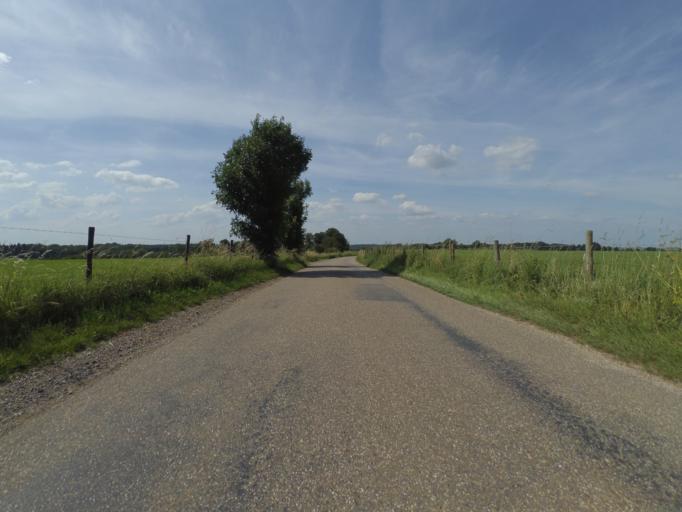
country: NL
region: Limburg
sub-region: Valkenburg aan de Geul
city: Schin op Geul
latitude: 50.7870
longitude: 5.8822
